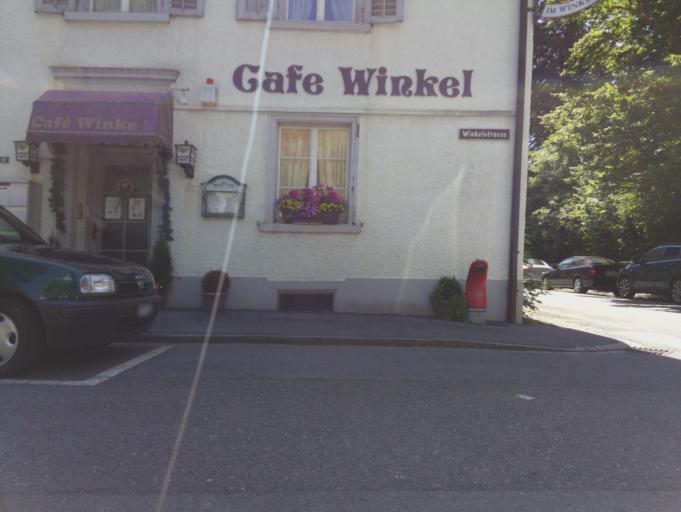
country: CH
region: Glarus
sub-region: Glarus
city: Glarus
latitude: 47.0433
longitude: 9.0665
